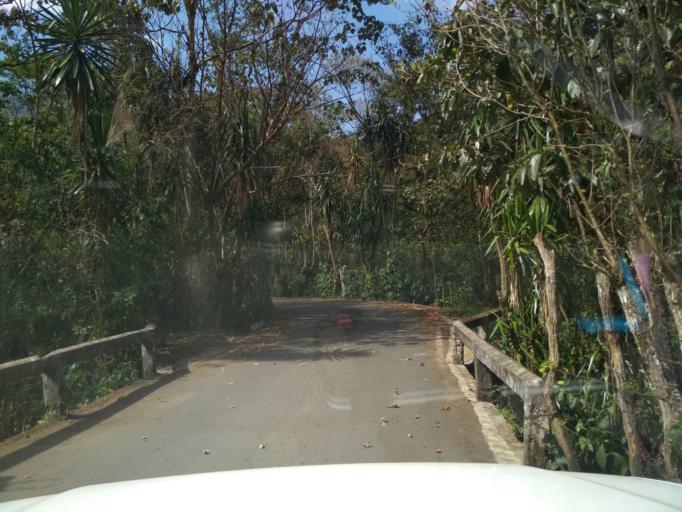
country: MX
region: Veracruz
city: Jalapilla
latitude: 18.7919
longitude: -97.1009
